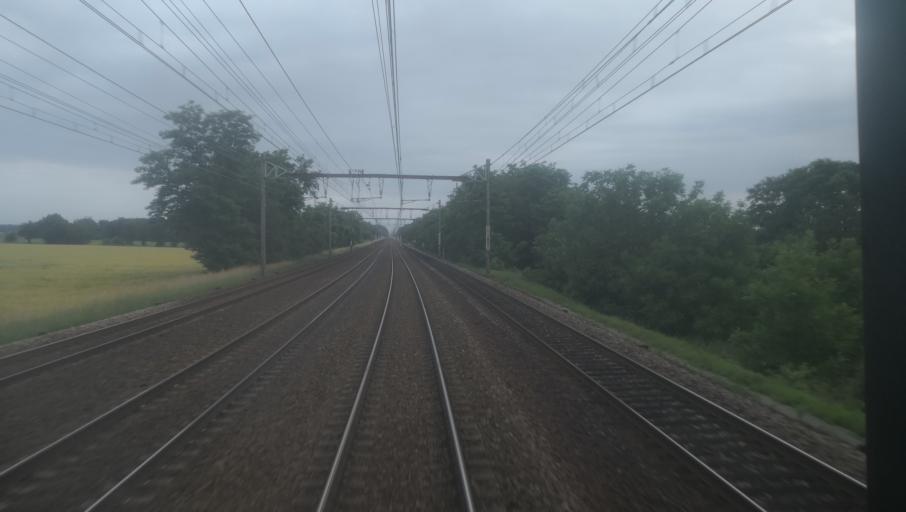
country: FR
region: Ile-de-France
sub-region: Departement de l'Essonne
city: Cheptainville
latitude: 48.5400
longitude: 2.2934
